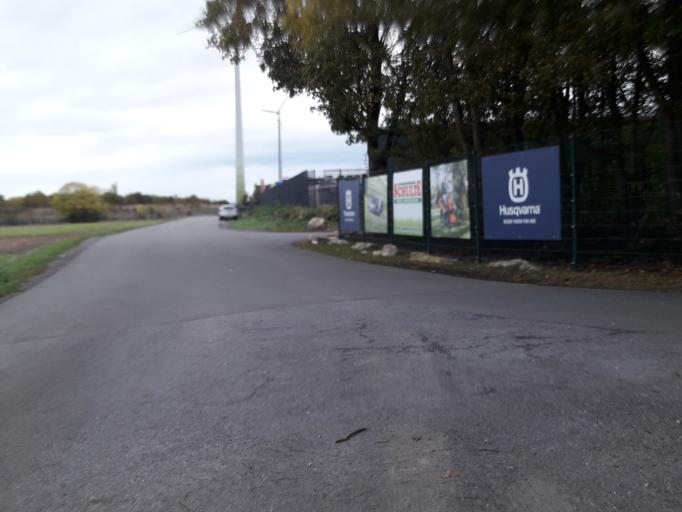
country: DE
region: North Rhine-Westphalia
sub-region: Regierungsbezirk Detmold
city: Paderborn
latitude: 51.6805
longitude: 8.7348
